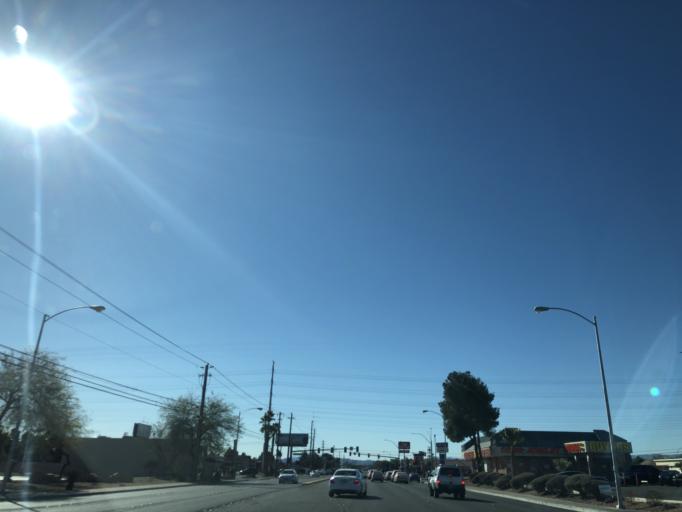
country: US
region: Nevada
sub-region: Clark County
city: Spring Valley
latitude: 36.1162
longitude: -115.2249
